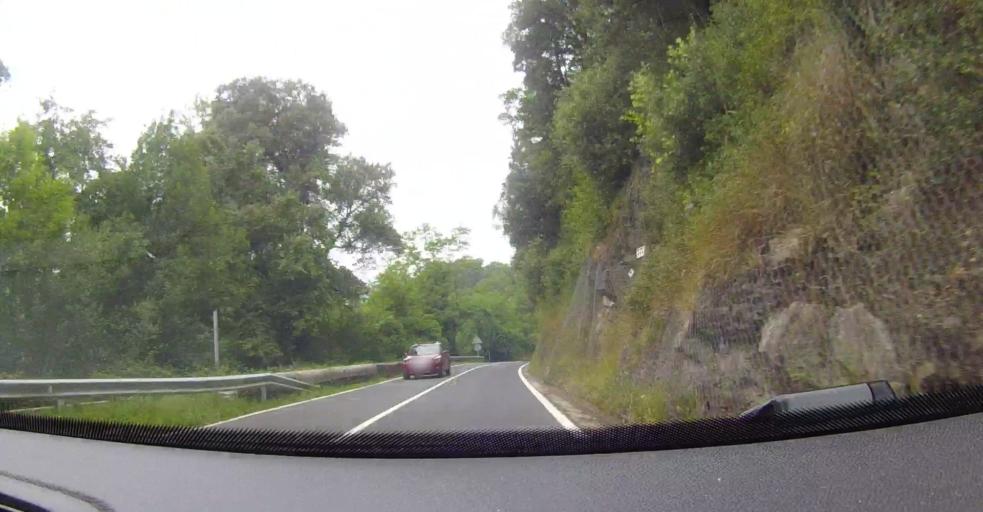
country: ES
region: Basque Country
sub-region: Bizkaia
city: Lanestosa
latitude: 43.2397
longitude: -3.3568
